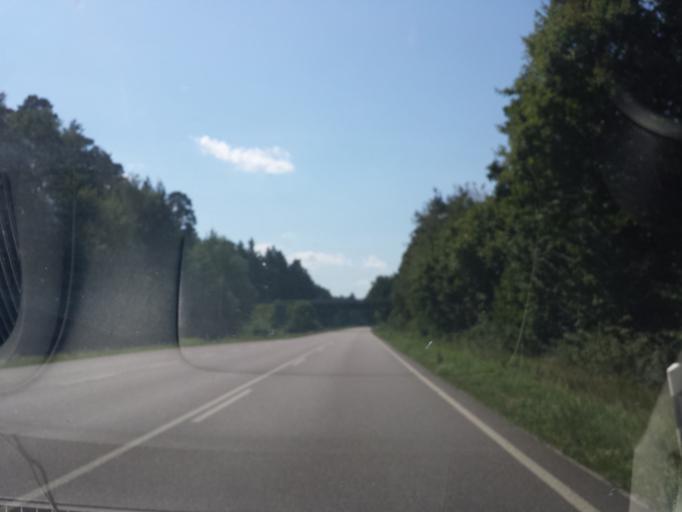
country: DE
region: Bavaria
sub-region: Upper Bavaria
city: Munchsmunster
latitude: 48.7545
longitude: 11.7034
